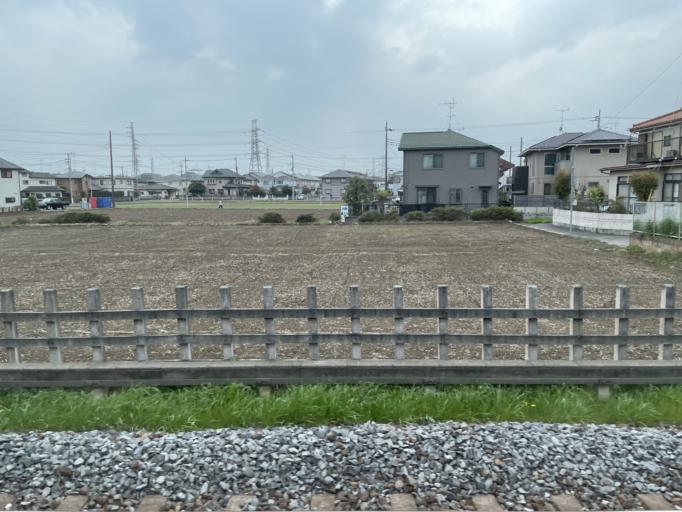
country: JP
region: Saitama
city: Kasukabe
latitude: 36.0014
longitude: 139.7398
